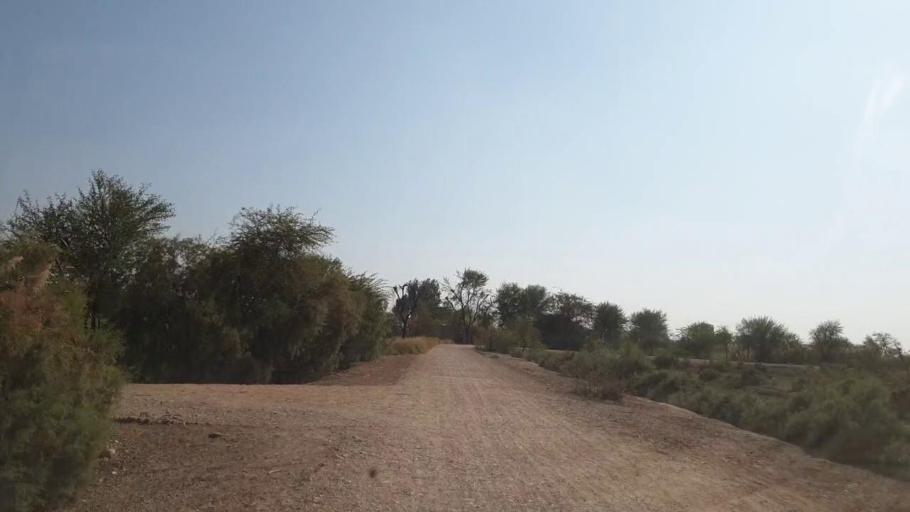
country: PK
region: Sindh
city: Mirpur Khas
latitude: 25.7193
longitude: 69.1613
